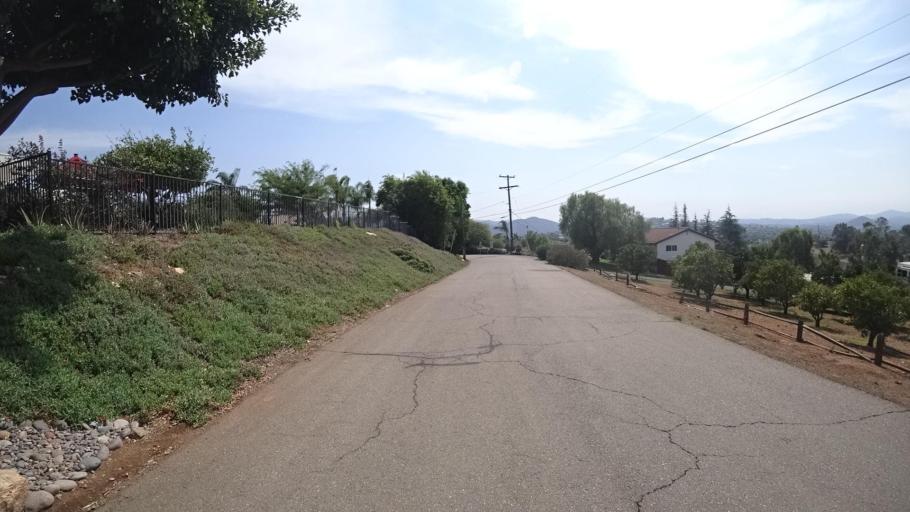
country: US
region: California
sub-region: San Diego County
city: Escondido
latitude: 33.0834
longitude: -117.0465
